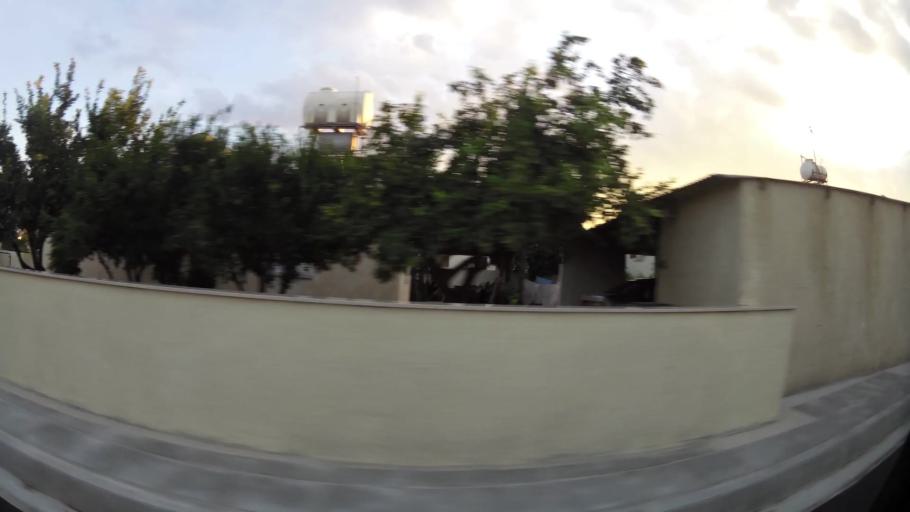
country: CY
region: Larnaka
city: Dhromolaxia
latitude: 34.8701
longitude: 33.5859
